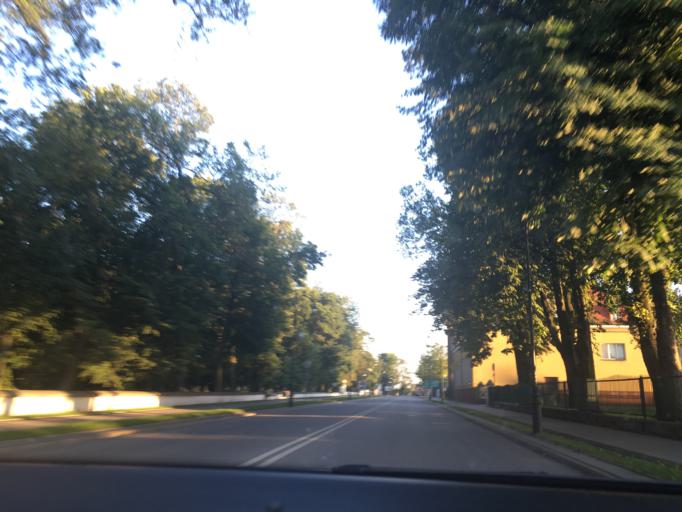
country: PL
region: Lublin Voivodeship
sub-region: Powiat radzynski
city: Radzyn Podlaski
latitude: 51.7857
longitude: 22.6224
